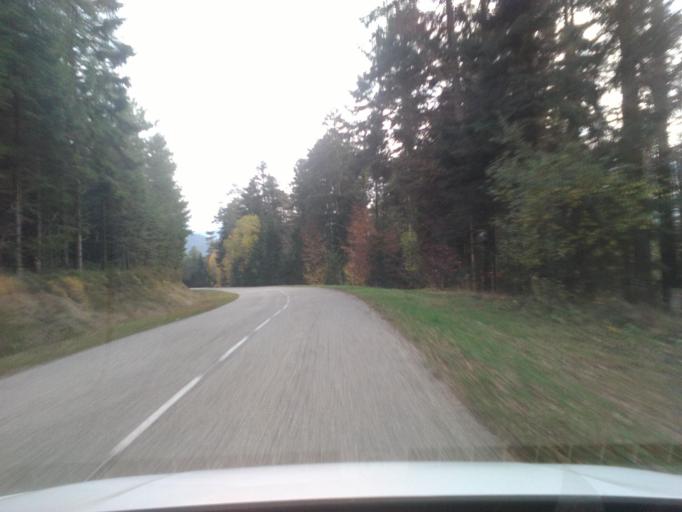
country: FR
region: Lorraine
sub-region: Departement des Vosges
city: Senones
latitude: 48.3689
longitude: 7.1057
